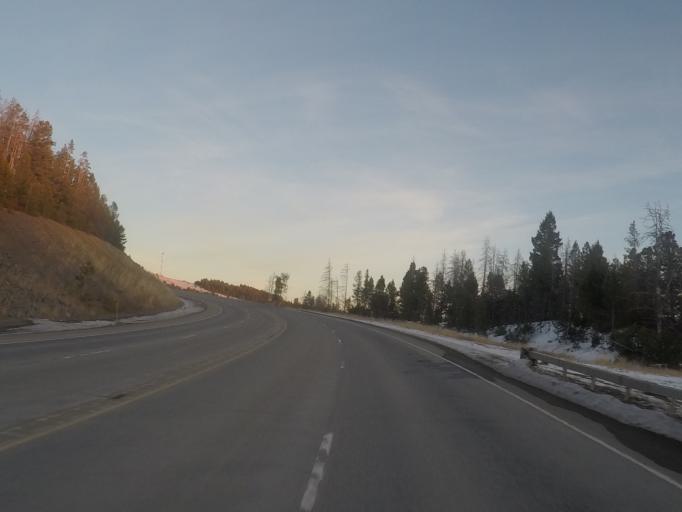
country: US
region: Montana
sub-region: Lewis and Clark County
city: Helena West Side
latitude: 46.5571
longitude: -112.3290
